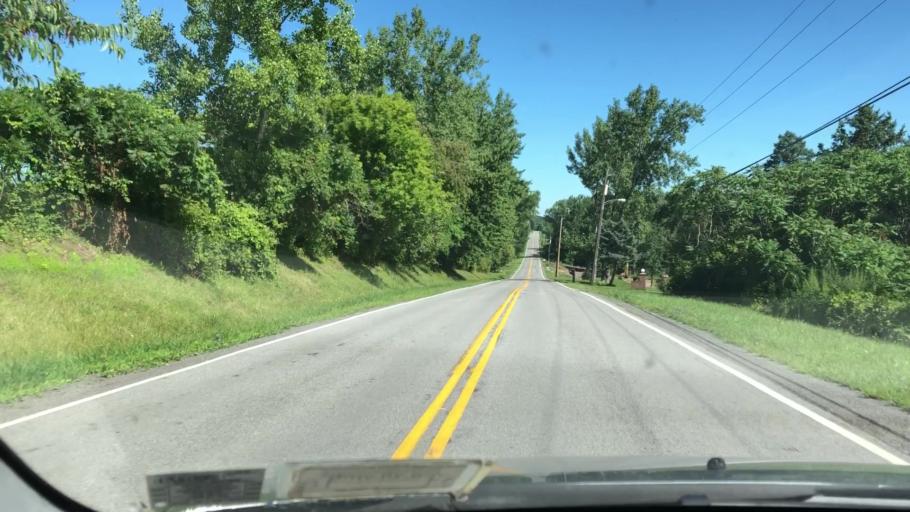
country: US
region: New York
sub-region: Monroe County
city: Fairport
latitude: 43.1111
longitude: -77.3730
